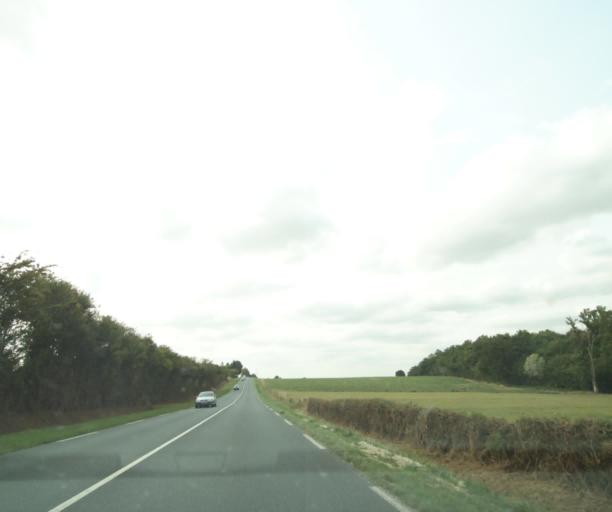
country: FR
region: Centre
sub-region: Departement de l'Indre
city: Buzancais
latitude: 46.9100
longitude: 1.3380
